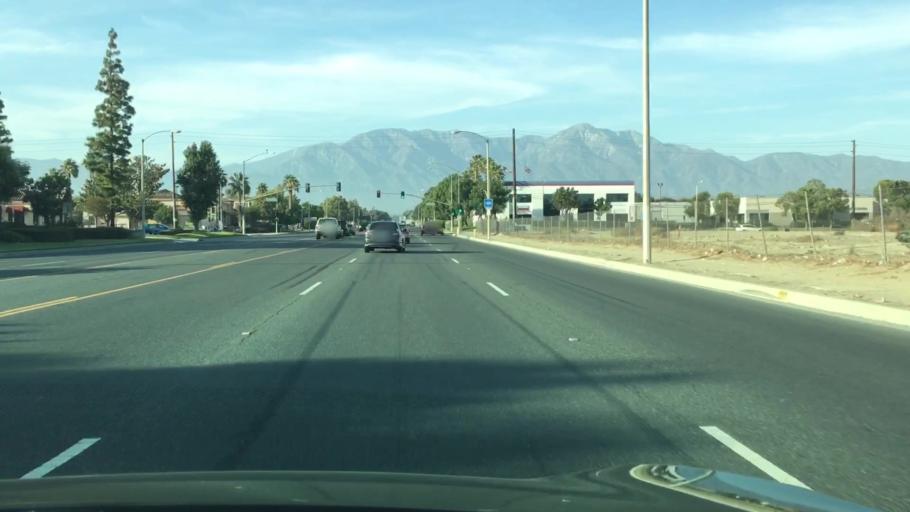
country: US
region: California
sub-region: San Bernardino County
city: Ontario
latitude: 34.0399
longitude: -117.6285
